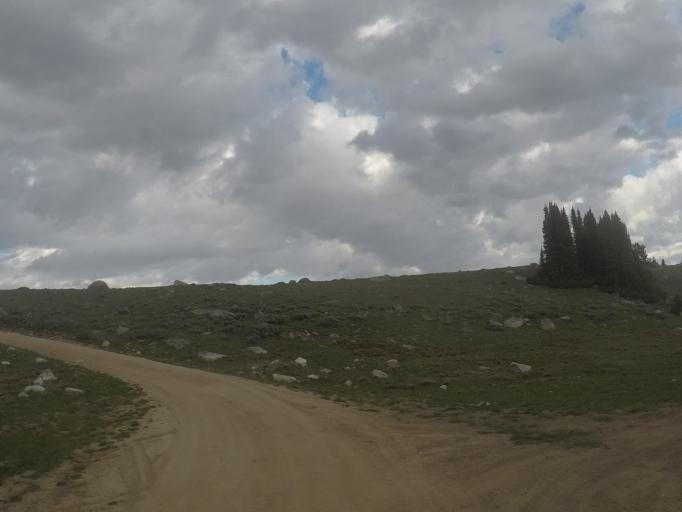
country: US
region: Wyoming
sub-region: Sheridan County
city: Sheridan
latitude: 44.5035
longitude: -107.4319
